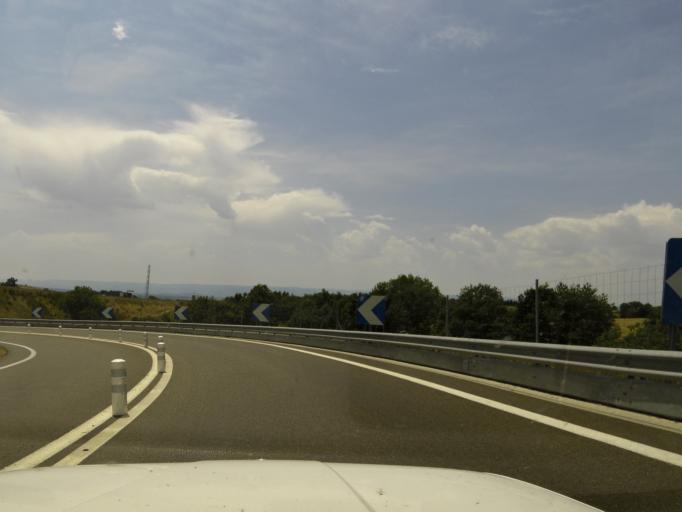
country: FR
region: Rhone-Alpes
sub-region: Departement de la Loire
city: Saint-Just-la-Pendue
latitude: 45.8525
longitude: 4.2230
